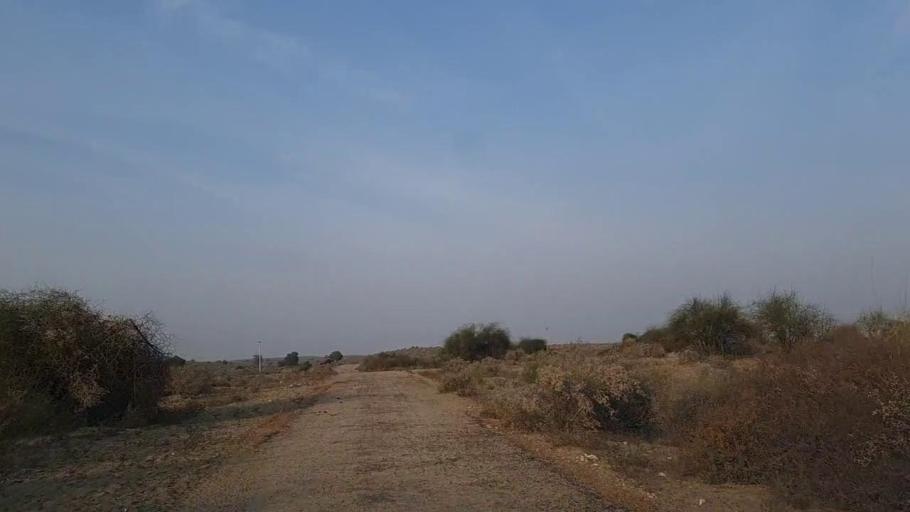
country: PK
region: Sindh
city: Jam Sahib
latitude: 26.4234
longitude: 68.6028
